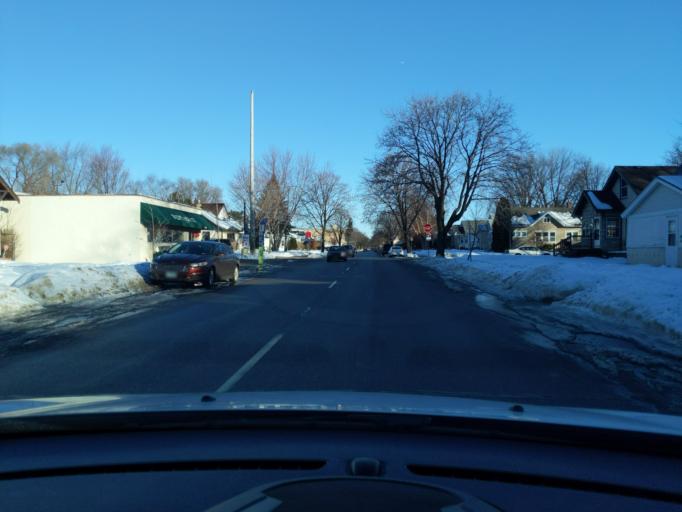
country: US
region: Minnesota
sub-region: Ramsey County
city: Lauderdale
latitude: 44.9320
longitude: -93.2128
